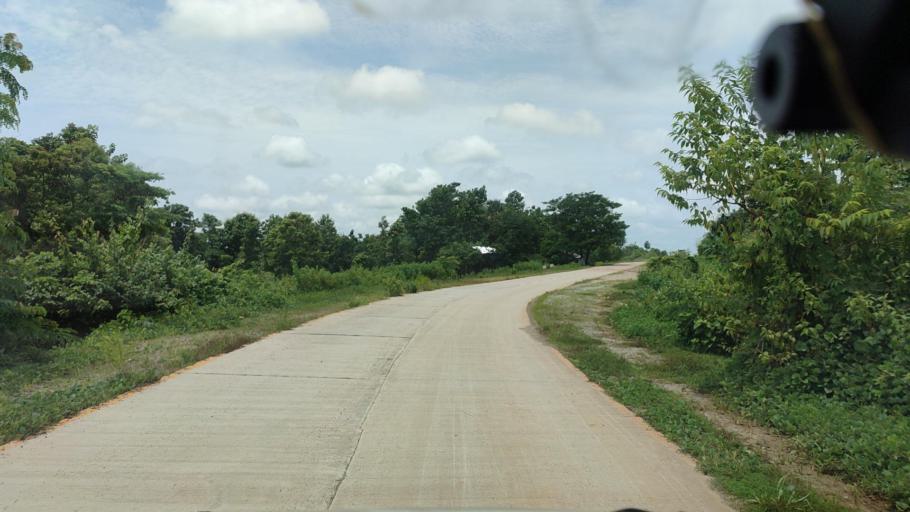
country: MM
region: Bago
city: Taungoo
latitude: 19.1371
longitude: 96.4600
